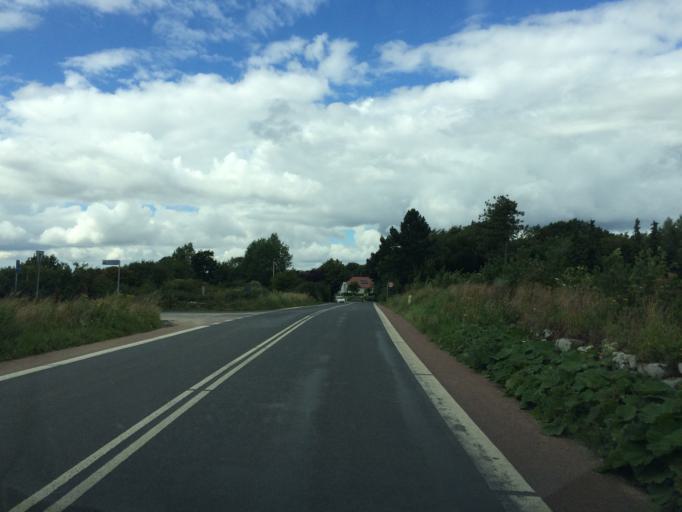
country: DK
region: South Denmark
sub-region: Assens Kommune
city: Harby
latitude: 55.1589
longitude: 10.1406
